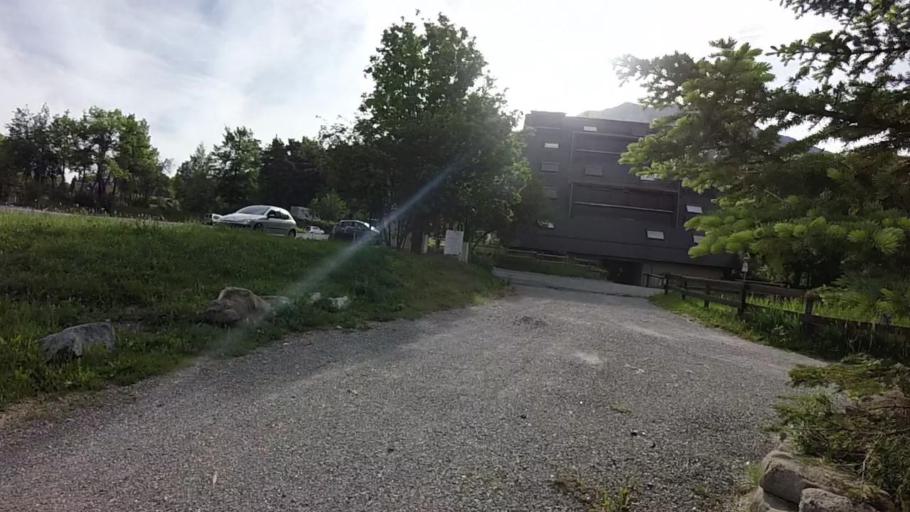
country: FR
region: Provence-Alpes-Cote d'Azur
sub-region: Departement des Alpes-de-Haute-Provence
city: Seyne-les-Alpes
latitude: 44.4130
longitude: 6.3509
